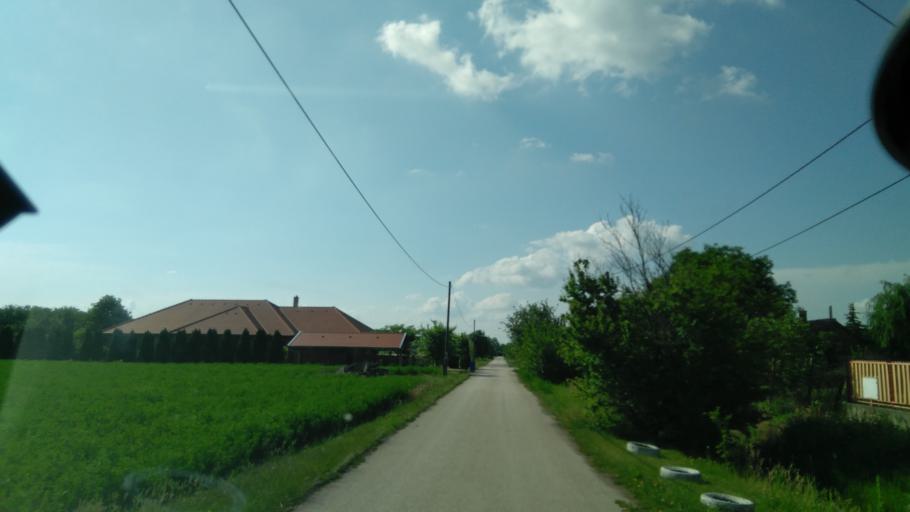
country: HU
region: Bekes
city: Doboz
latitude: 46.7017
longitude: 21.1786
